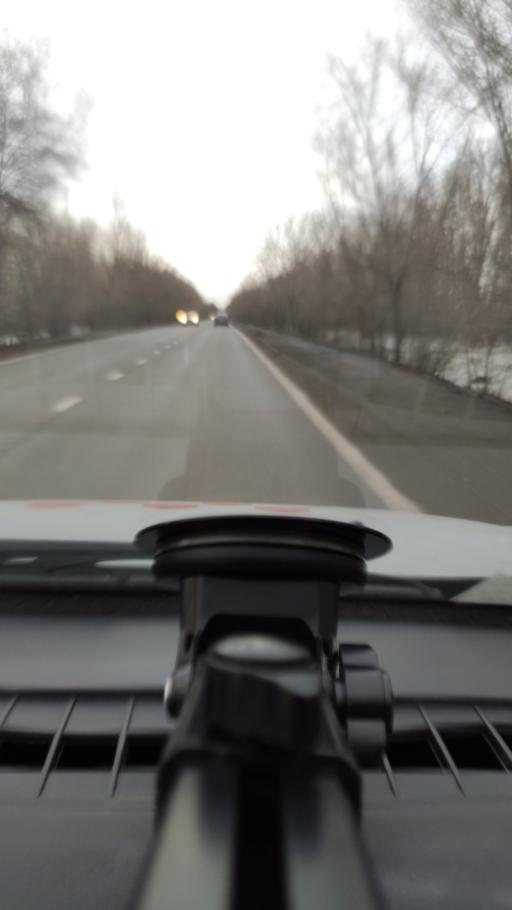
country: RU
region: Samara
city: Tol'yatti
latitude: 53.5464
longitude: 49.3936
